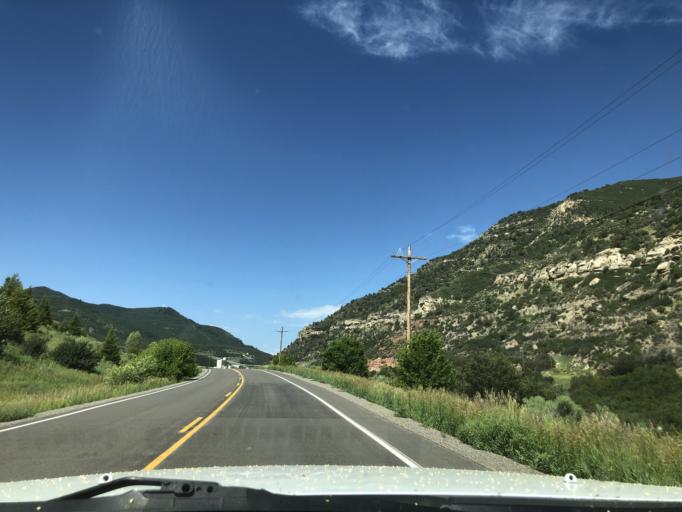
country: US
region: Colorado
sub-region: Delta County
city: Paonia
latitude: 38.9304
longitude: -107.4170
